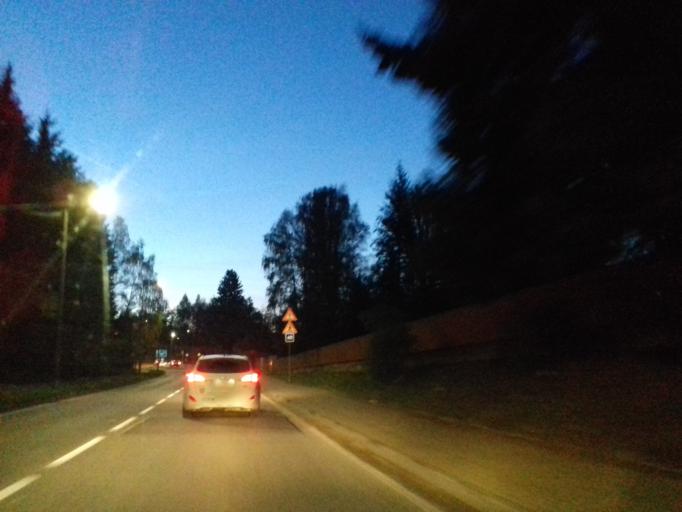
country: CZ
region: Vysocina
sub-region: Okres Pelhrimov
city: Humpolec
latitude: 49.5350
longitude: 15.3568
